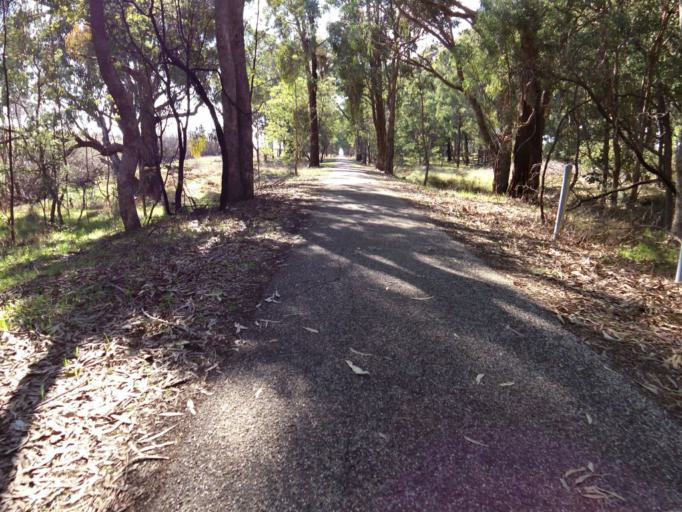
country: AU
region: Victoria
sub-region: Wangaratta
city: Wangaratta
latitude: -36.4017
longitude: 146.6434
